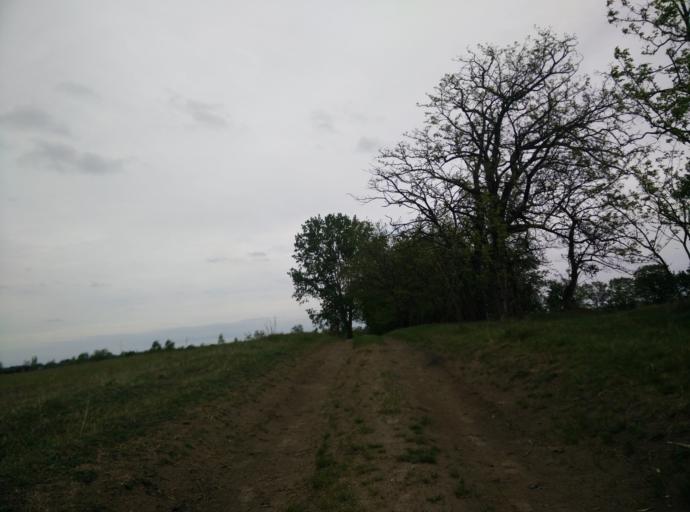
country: HU
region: Pest
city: Dunakeszi
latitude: 47.6052
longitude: 19.1424
